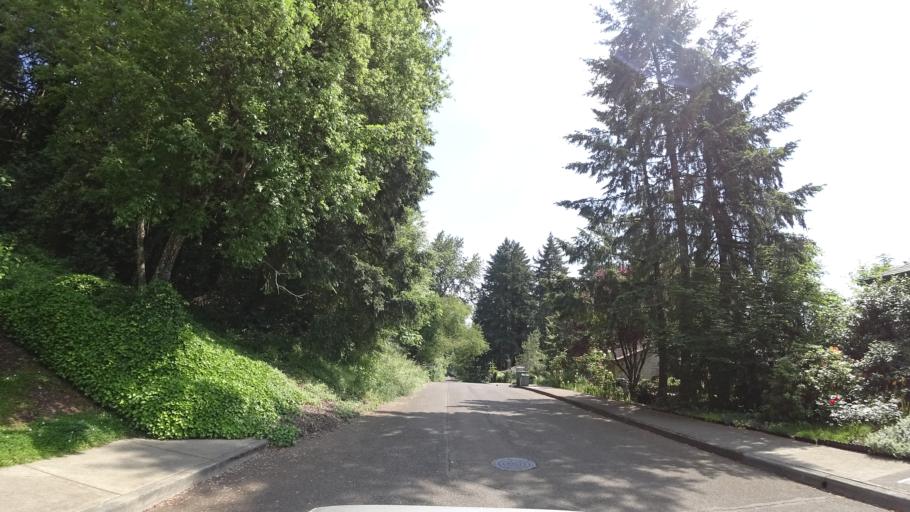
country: US
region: Oregon
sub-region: Washington County
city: Metzger
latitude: 45.4511
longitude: -122.7360
